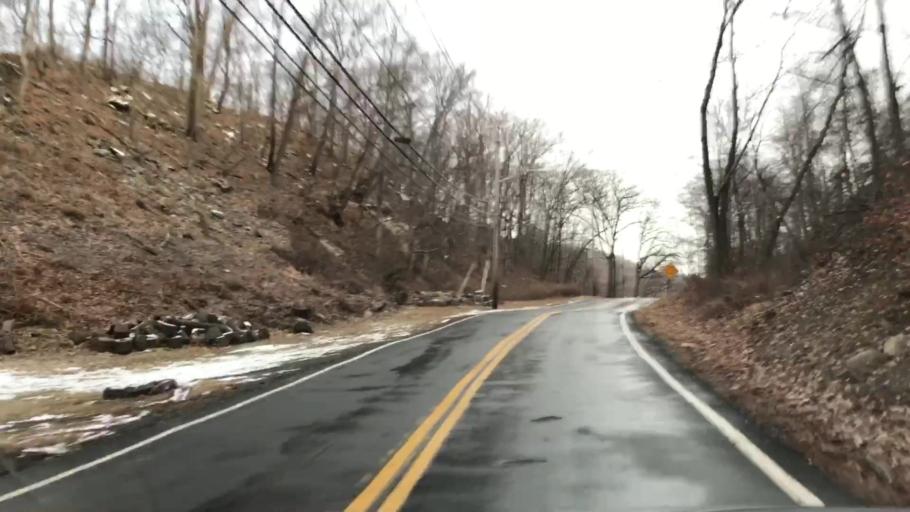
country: US
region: New York
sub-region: Rockland County
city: Thiells
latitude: 41.2240
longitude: -74.0468
